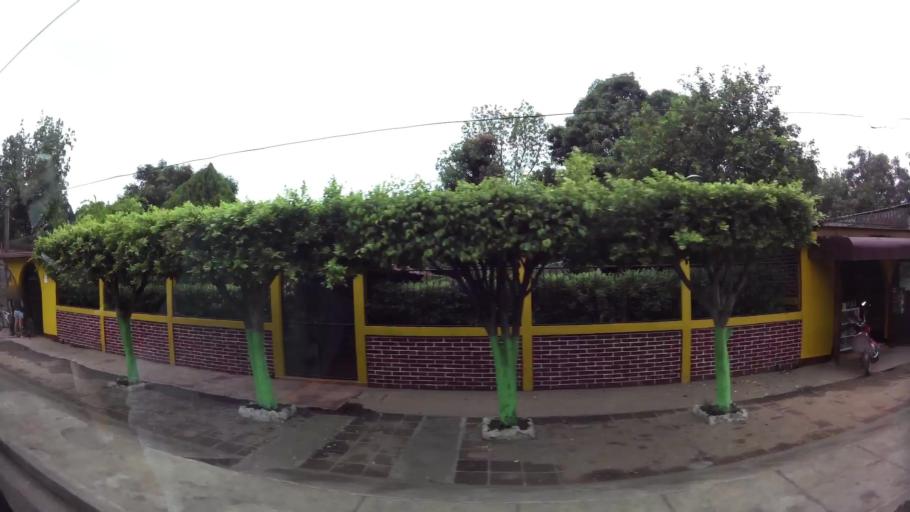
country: NI
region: Chinandega
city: Chinandega
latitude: 12.6188
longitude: -87.1211
